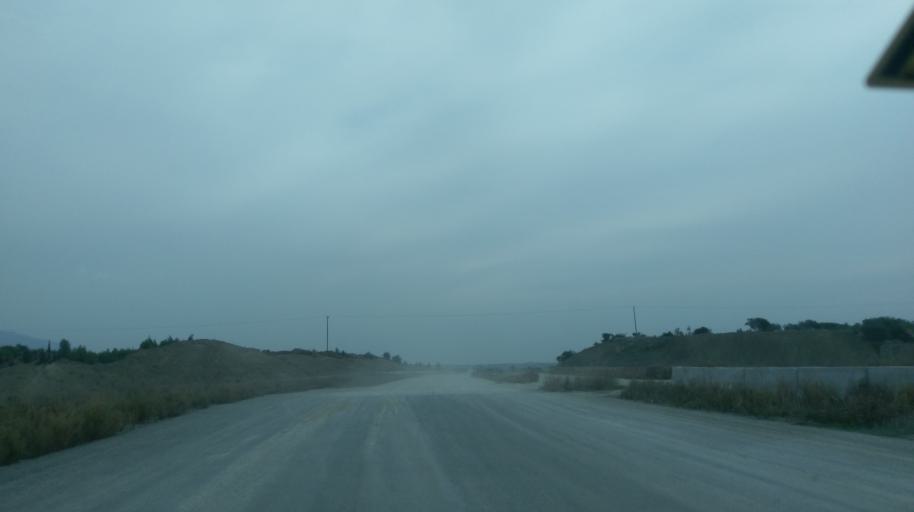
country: CY
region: Lefkosia
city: Nicosia
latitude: 35.2370
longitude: 33.3261
